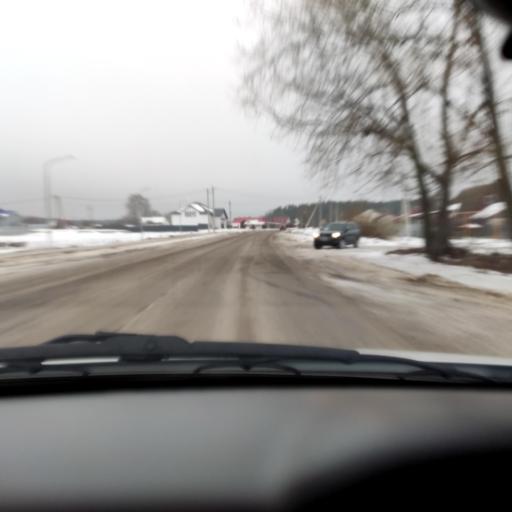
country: RU
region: Voronezj
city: Ramon'
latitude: 51.9049
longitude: 39.2859
